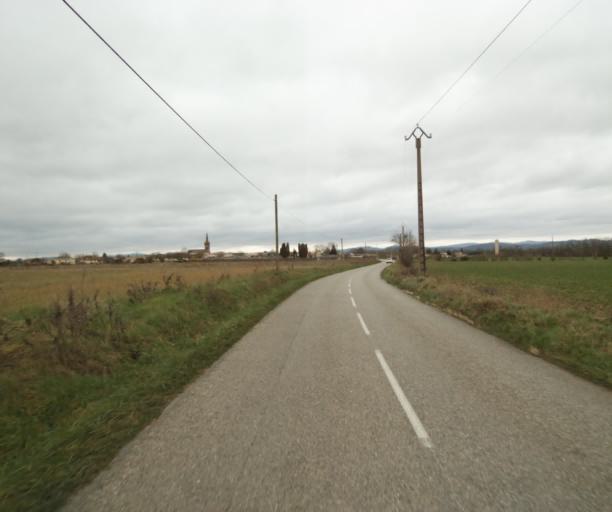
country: FR
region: Midi-Pyrenees
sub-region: Departement de l'Ariege
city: Pamiers
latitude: 43.1593
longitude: 1.6363
